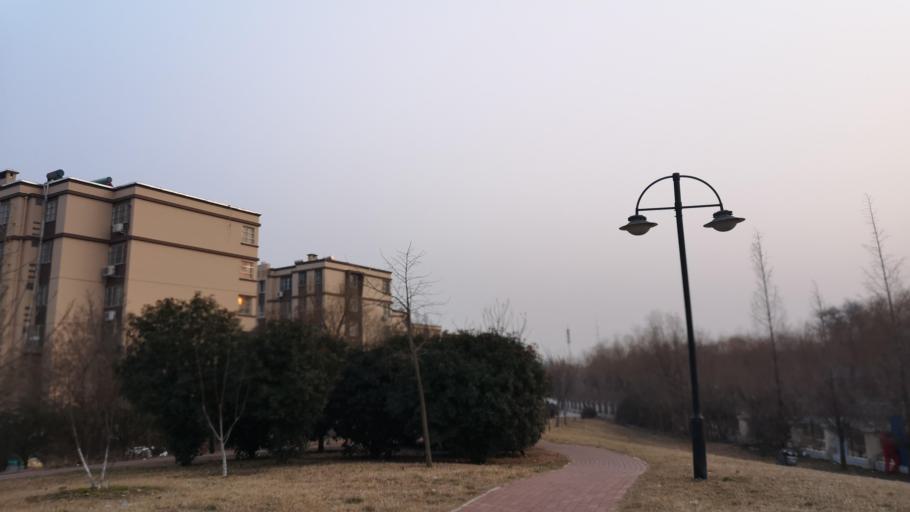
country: CN
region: Henan Sheng
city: Zhongyuanlu
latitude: 35.7888
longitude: 115.0749
